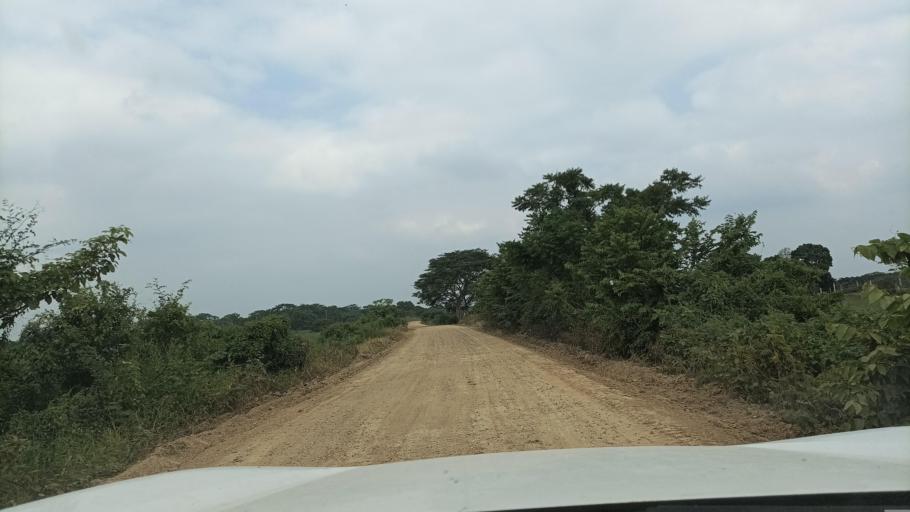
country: MX
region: Veracruz
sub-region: Texistepec
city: San Lorenzo Tenochtitlan
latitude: 17.7787
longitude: -94.7929
